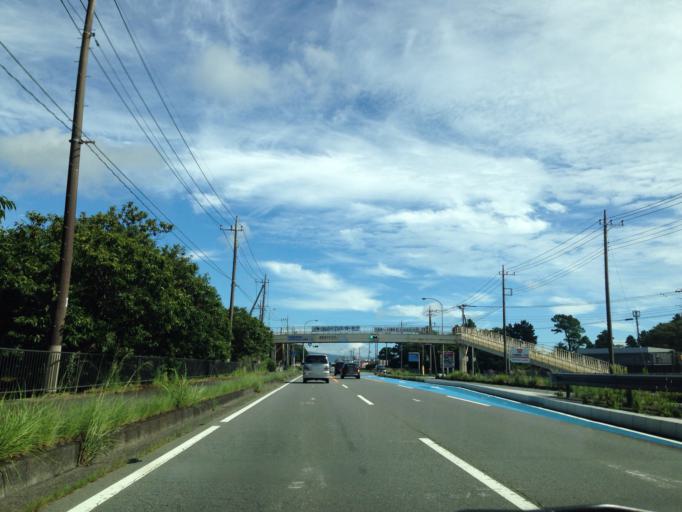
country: JP
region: Shizuoka
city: Gotemba
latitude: 35.2873
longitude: 138.9193
